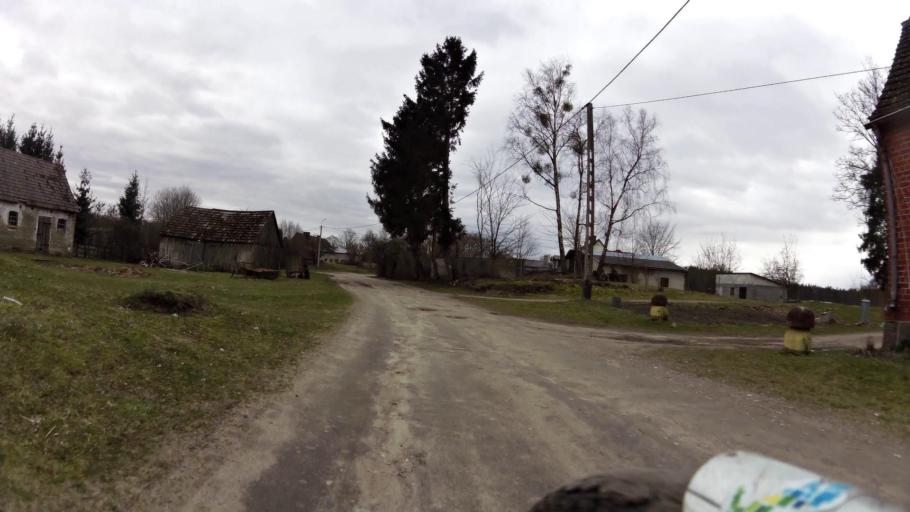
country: PL
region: Pomeranian Voivodeship
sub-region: Powiat bytowski
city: Trzebielino
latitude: 54.1071
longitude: 17.1300
